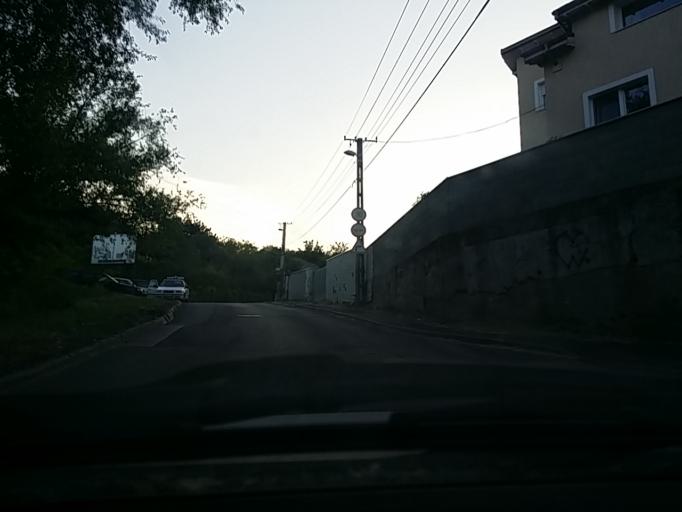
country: HU
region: Pest
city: Urom
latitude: 47.5883
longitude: 19.0356
